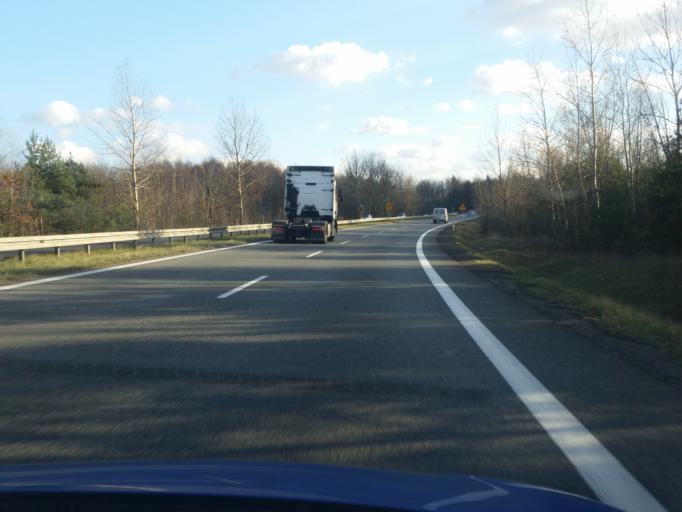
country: PL
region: Silesian Voivodeship
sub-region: Powiat bedzinski
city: Siewierz
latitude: 50.4872
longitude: 19.2159
